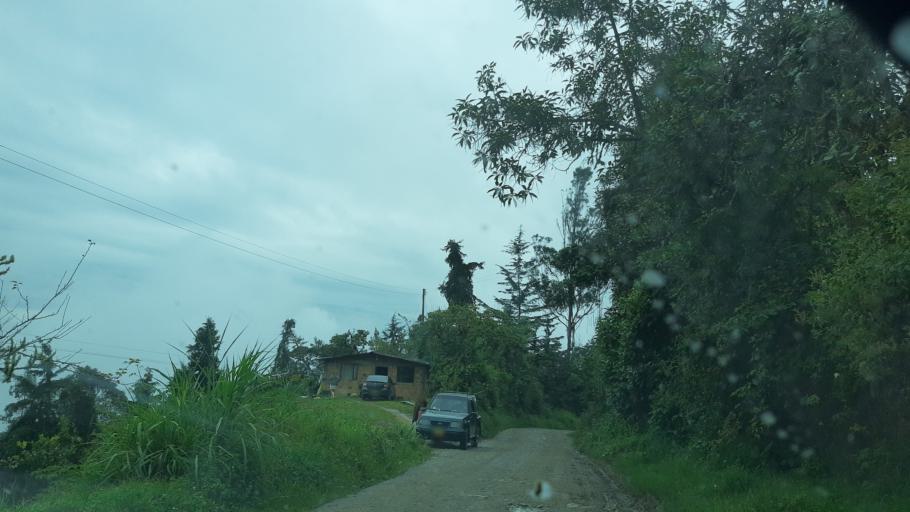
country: CO
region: Cundinamarca
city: Tenza
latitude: 5.0387
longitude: -73.4328
